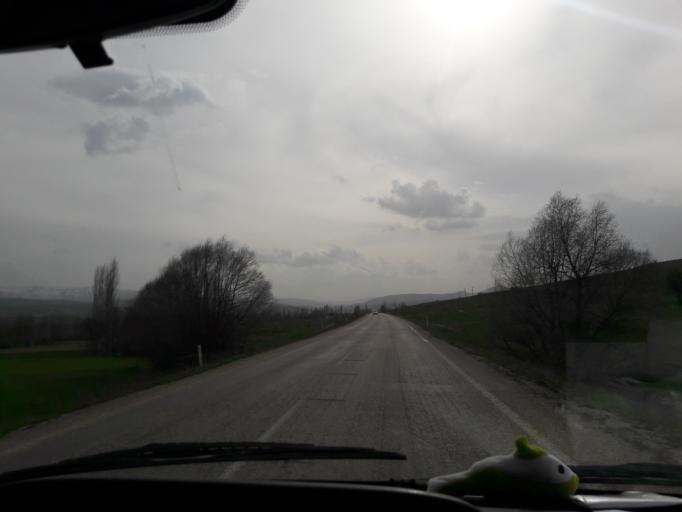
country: TR
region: Gumushane
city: Siran
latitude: 40.1705
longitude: 39.0708
